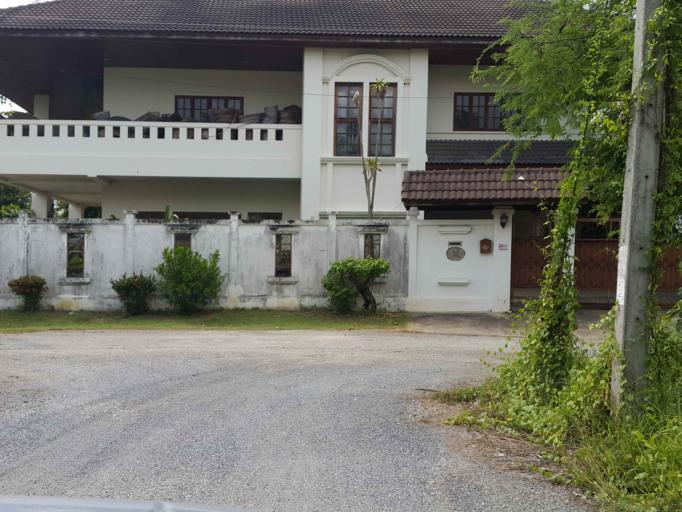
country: TH
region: Chiang Mai
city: San Kamphaeng
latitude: 18.7670
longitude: 99.0700
